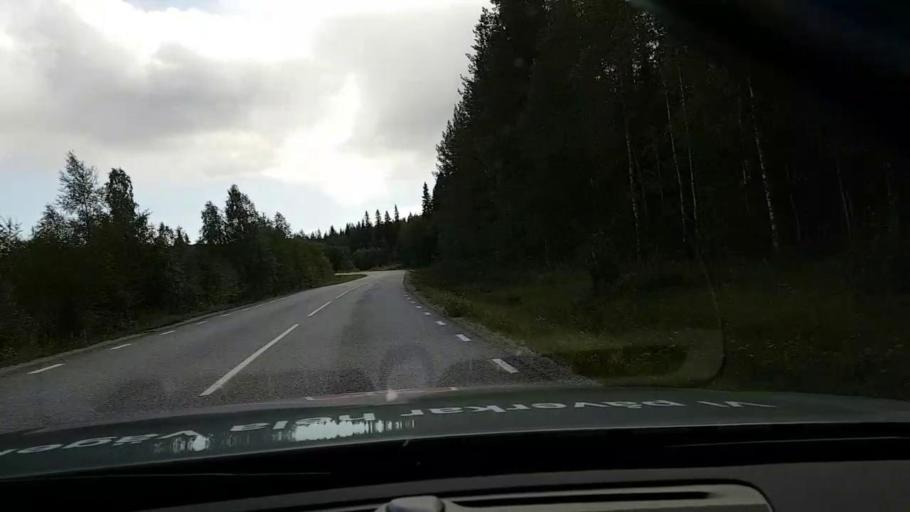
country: SE
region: Vaesternorrland
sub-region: OErnskoeldsviks Kommun
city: Bredbyn
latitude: 63.6893
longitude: 17.7706
